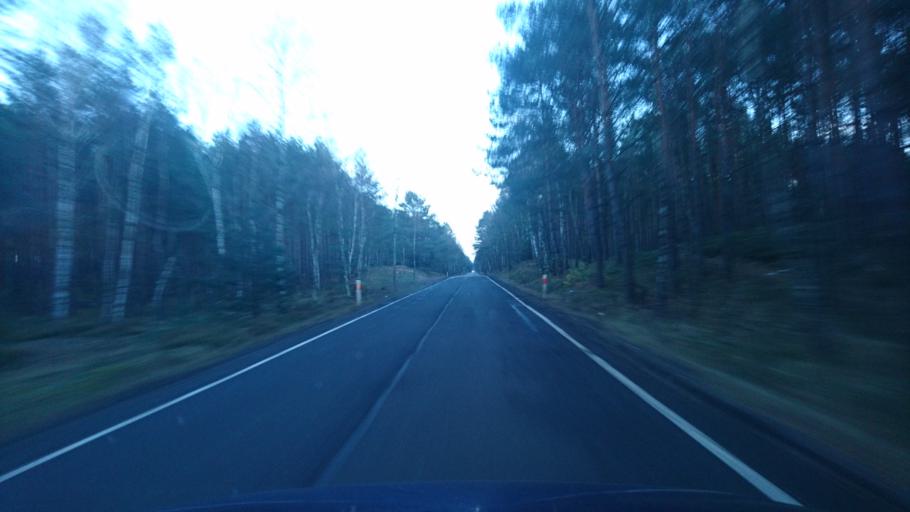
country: PL
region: Greater Poland Voivodeship
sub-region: Powiat ostrowski
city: Jankow Przygodzki
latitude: 51.5304
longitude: 17.7467
